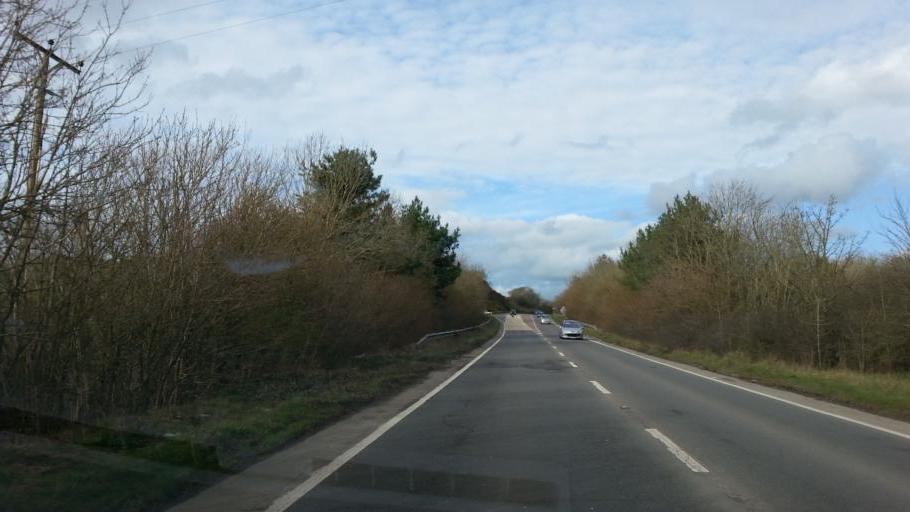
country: GB
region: England
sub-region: Devon
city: Northam
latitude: 51.0244
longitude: -4.2325
